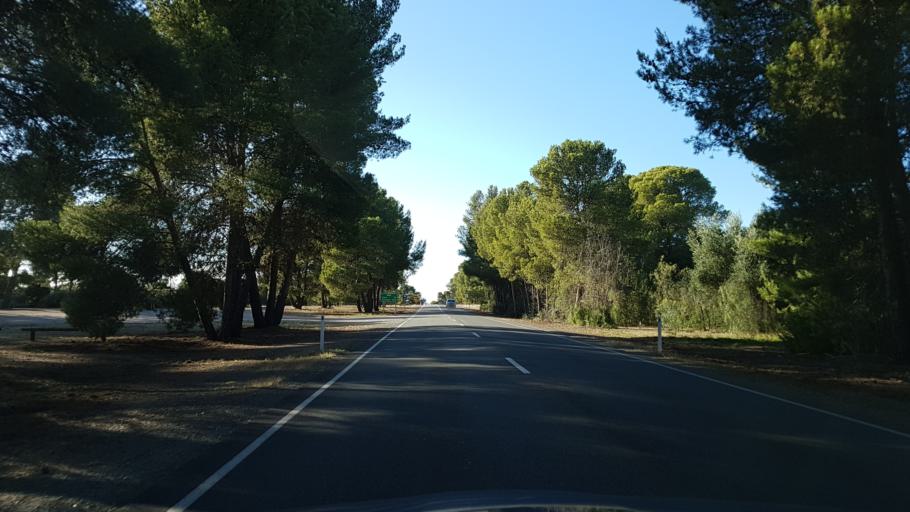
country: AU
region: South Australia
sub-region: Port Pirie City and Dists
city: Crystal Brook
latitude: -33.2679
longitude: 138.3491
